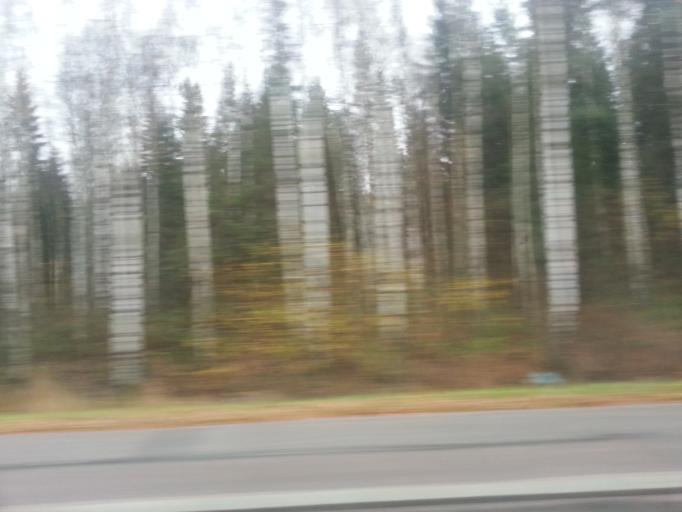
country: FI
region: Uusimaa
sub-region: Helsinki
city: Vantaa
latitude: 60.3008
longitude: 24.9514
